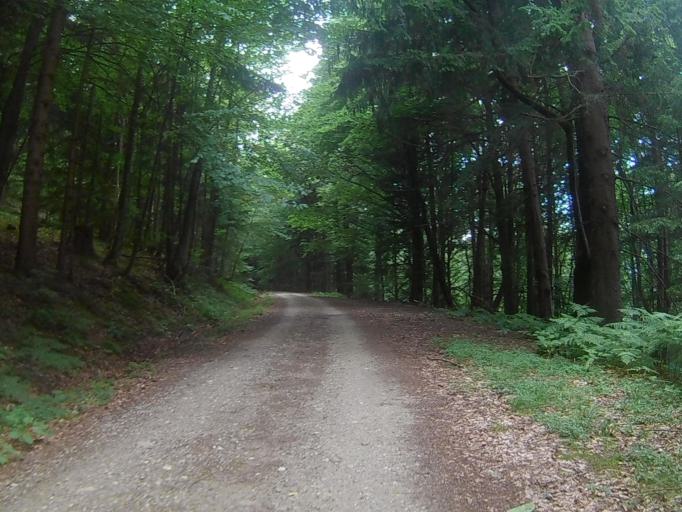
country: SI
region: Selnica ob Dravi
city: Selnica ob Dravi
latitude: 46.5221
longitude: 15.4833
